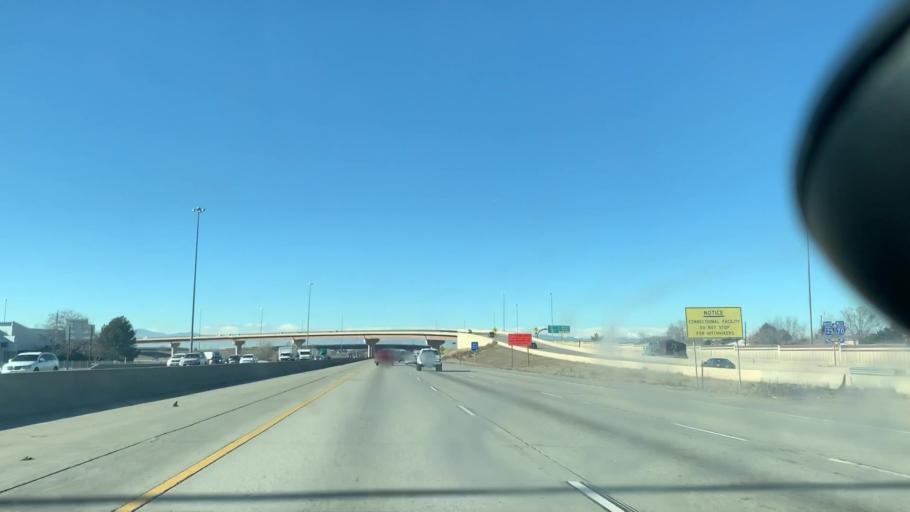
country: US
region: Colorado
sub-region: Adams County
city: Aurora
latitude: 39.7719
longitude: -104.8202
